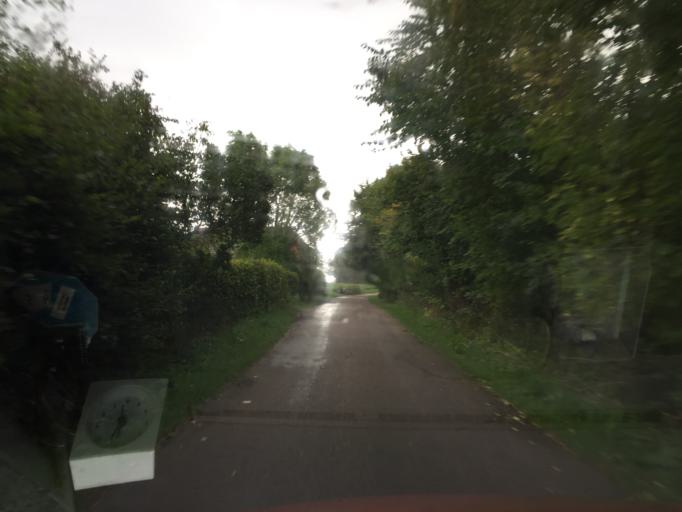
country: DK
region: South Denmark
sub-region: Sonderborg Kommune
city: Dybbol
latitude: 54.9556
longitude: 9.7391
